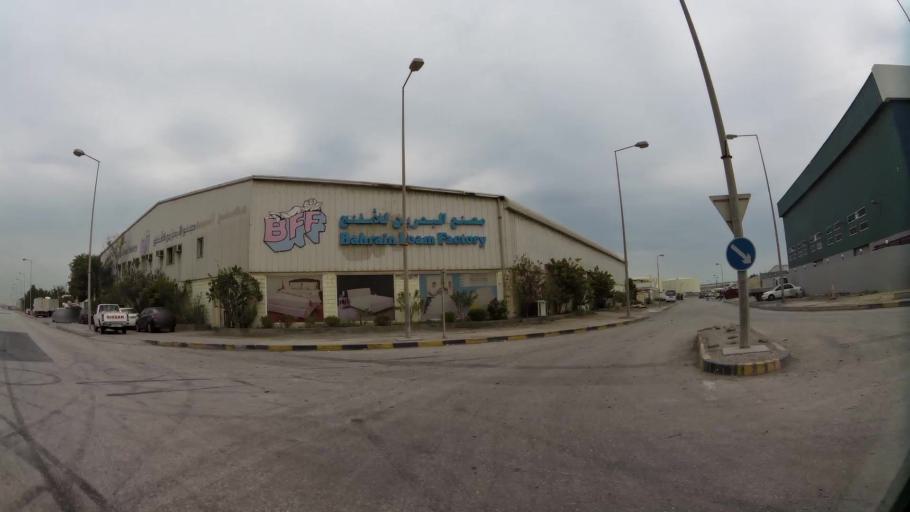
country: BH
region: Northern
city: Sitrah
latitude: 26.1804
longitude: 50.6155
